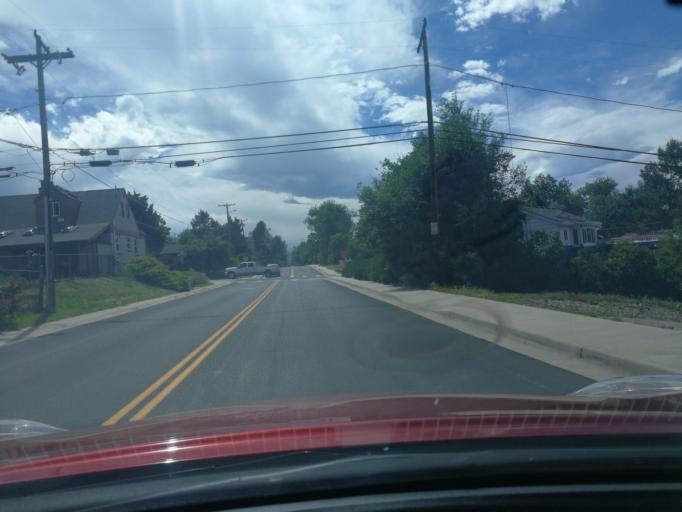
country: US
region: Colorado
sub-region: Arapahoe County
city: Littleton
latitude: 39.6151
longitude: -104.9965
